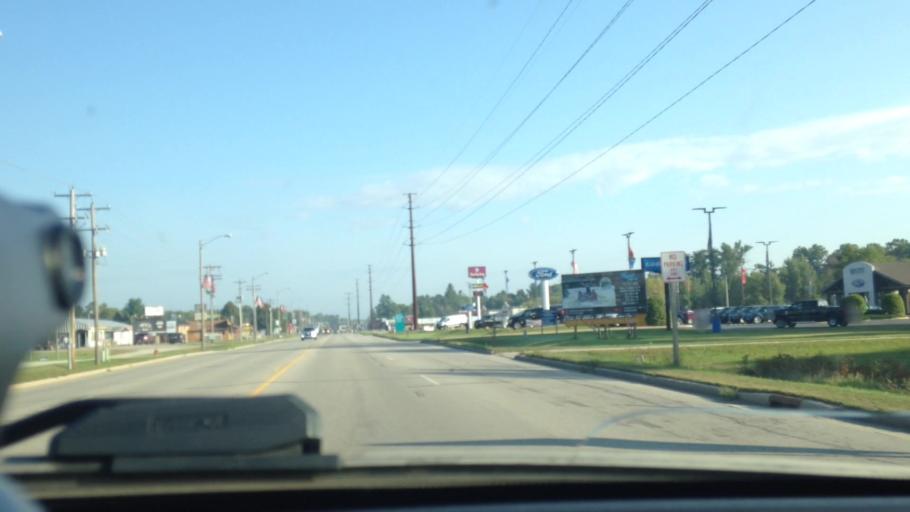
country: US
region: Wisconsin
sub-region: Marinette County
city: Peshtigo
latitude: 45.2254
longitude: -87.9968
